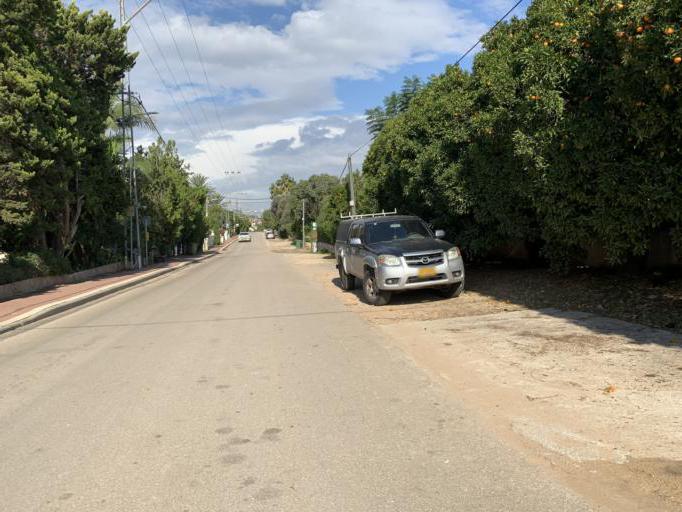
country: IL
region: Central District
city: Ra'anana
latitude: 32.1689
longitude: 34.8754
